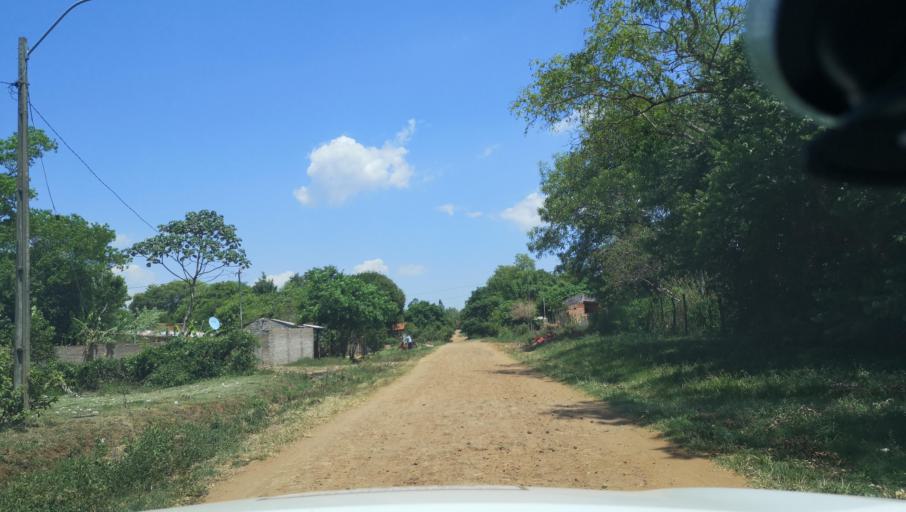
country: PY
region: Itapua
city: Carmen del Parana
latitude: -27.1660
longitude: -56.2445
